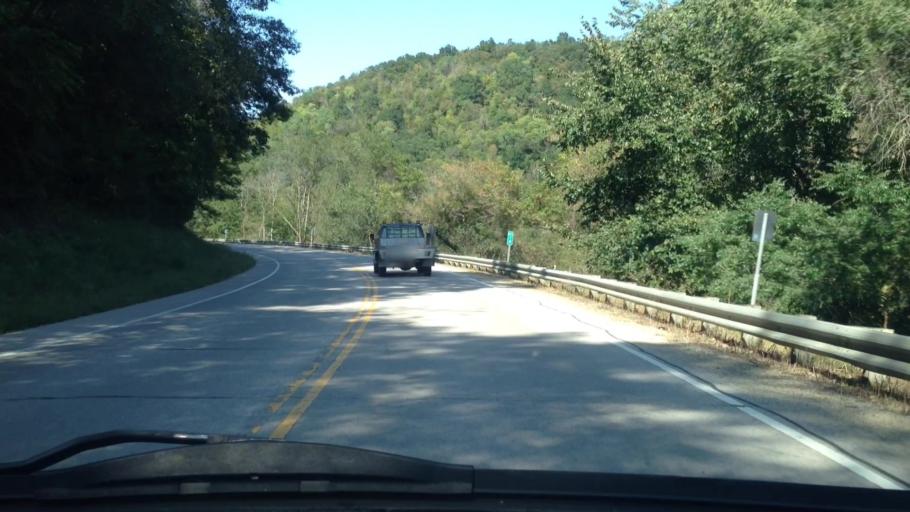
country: US
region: Minnesota
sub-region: Fillmore County
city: Rushford
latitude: 43.7653
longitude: -91.7633
